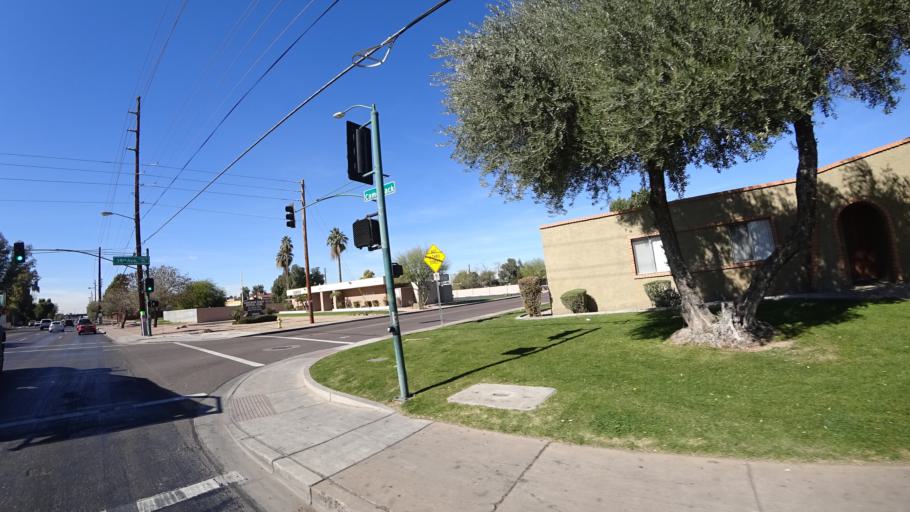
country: US
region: Arizona
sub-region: Maricopa County
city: Glendale
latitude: 33.5095
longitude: -112.1426
